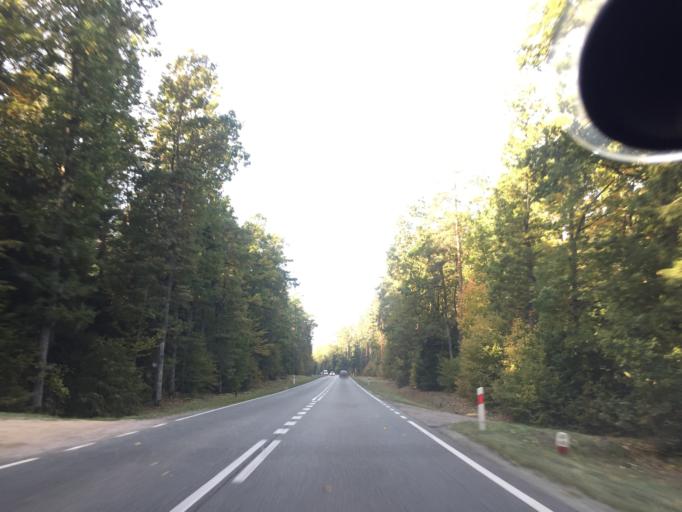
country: PL
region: Warmian-Masurian Voivodeship
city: Dobre Miasto
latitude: 54.0653
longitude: 20.4616
